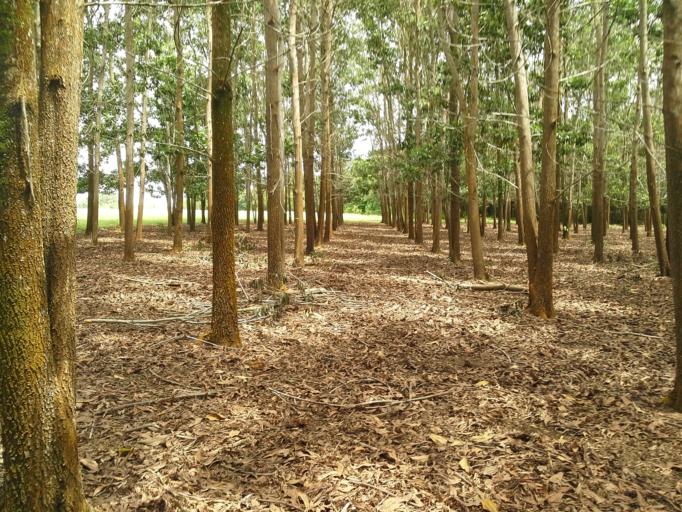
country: CO
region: Cundinamarca
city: Tibacuy
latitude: 4.2125
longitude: -72.4433
